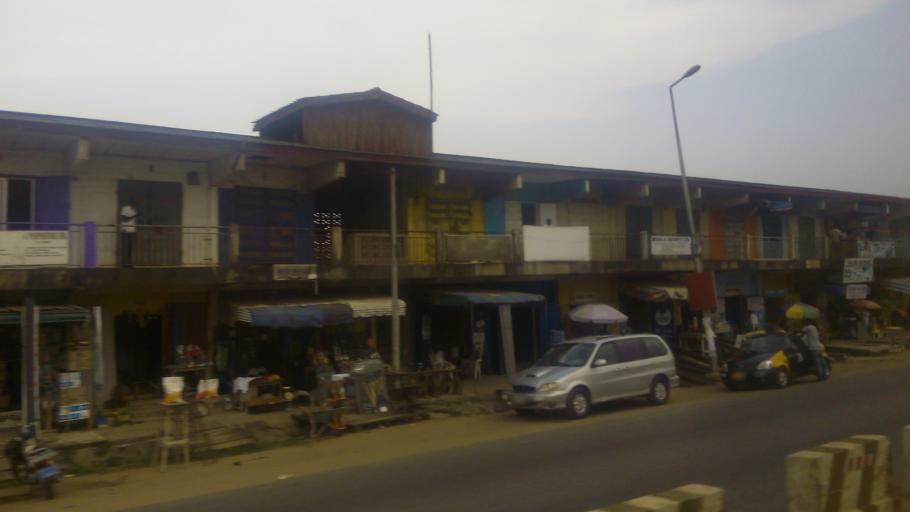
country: GH
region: Western
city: Takoradi
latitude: 4.8987
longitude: -1.7662
